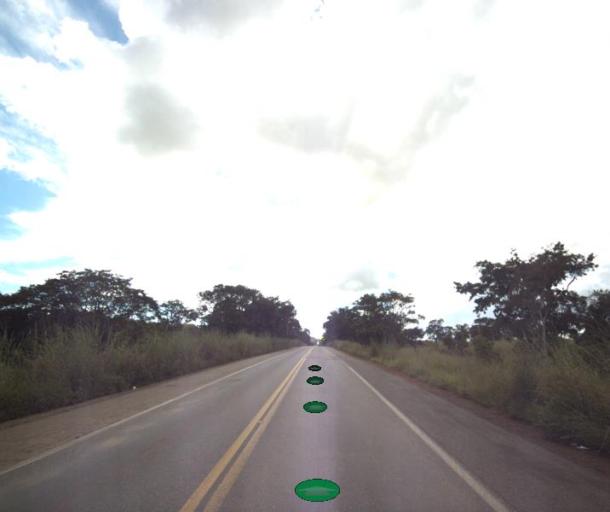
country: BR
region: Goias
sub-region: Jaragua
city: Jaragua
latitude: -15.9208
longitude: -49.2160
